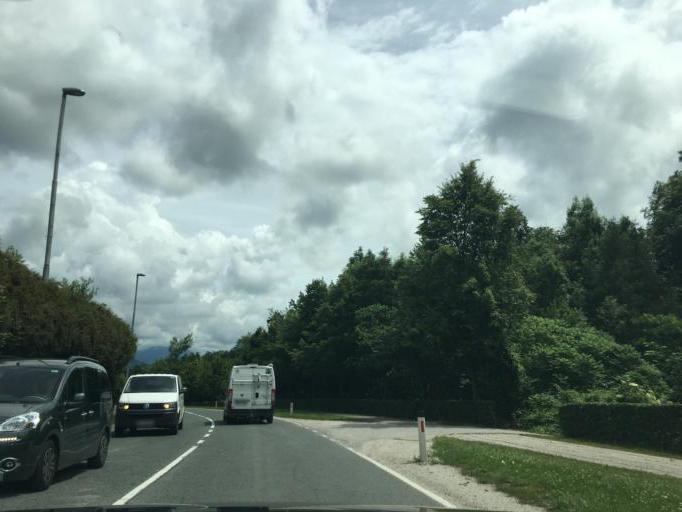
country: SI
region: Bled
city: Bled
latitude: 46.3671
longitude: 14.1222
